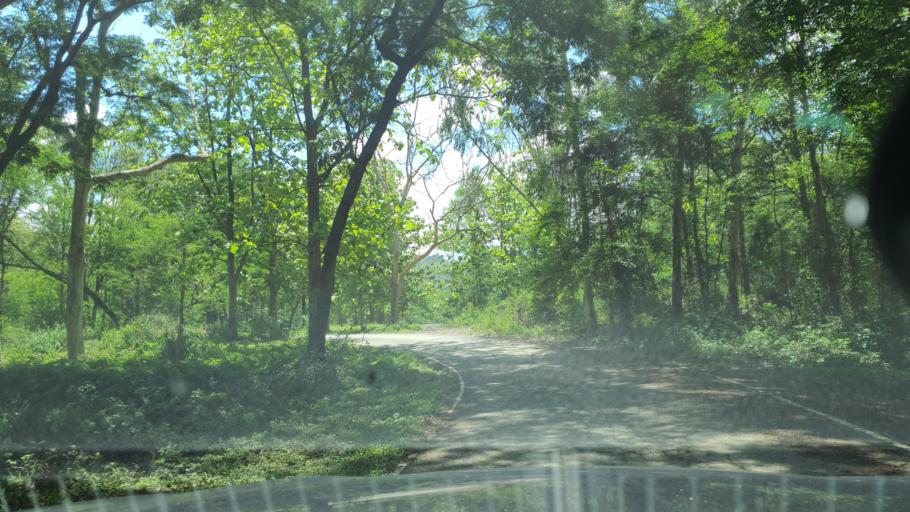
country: TH
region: Chiang Mai
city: Mae On
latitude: 18.8132
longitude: 99.2645
